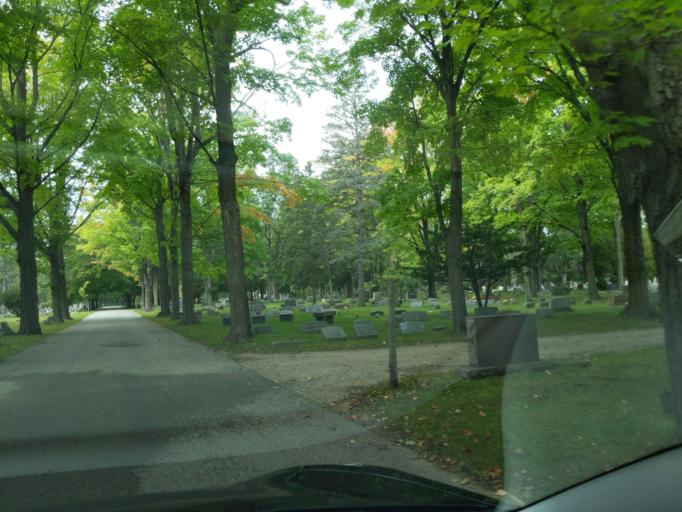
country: US
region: Michigan
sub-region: Grand Traverse County
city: Traverse City
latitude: 44.7545
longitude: -85.5863
